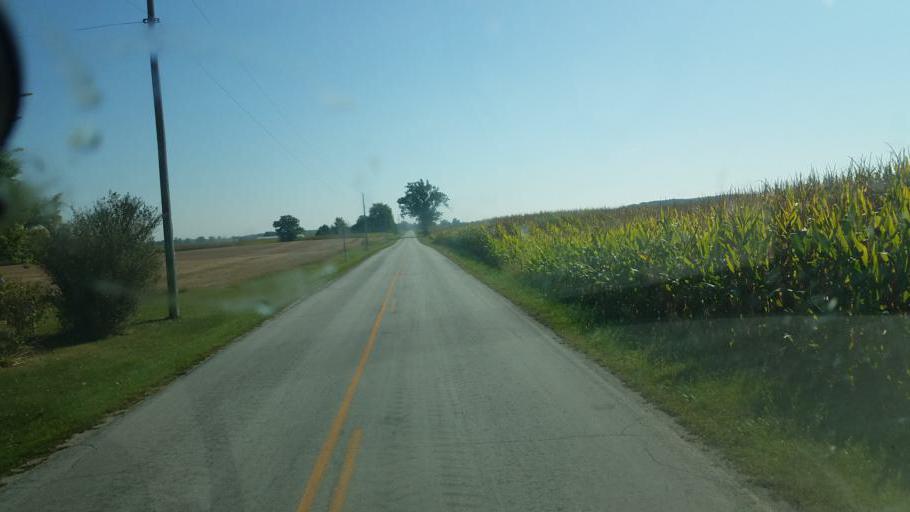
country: US
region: Ohio
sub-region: Hardin County
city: Kenton
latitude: 40.6122
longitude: -83.5823
